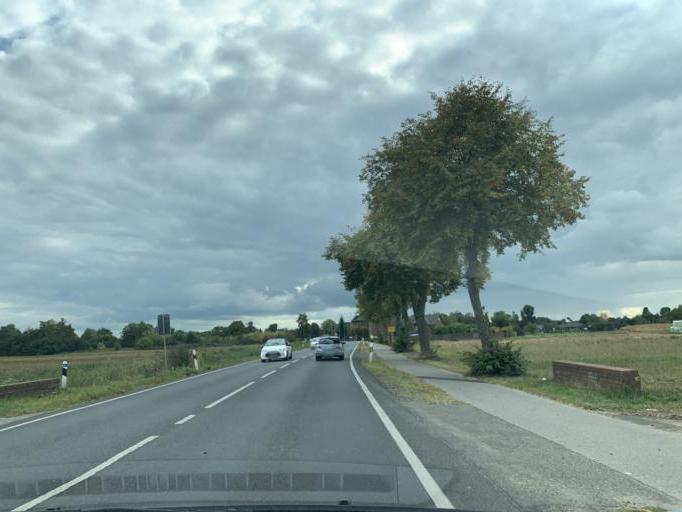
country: DE
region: North Rhine-Westphalia
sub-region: Regierungsbezirk Koln
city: Wassenberg
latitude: 51.0921
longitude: 6.1513
